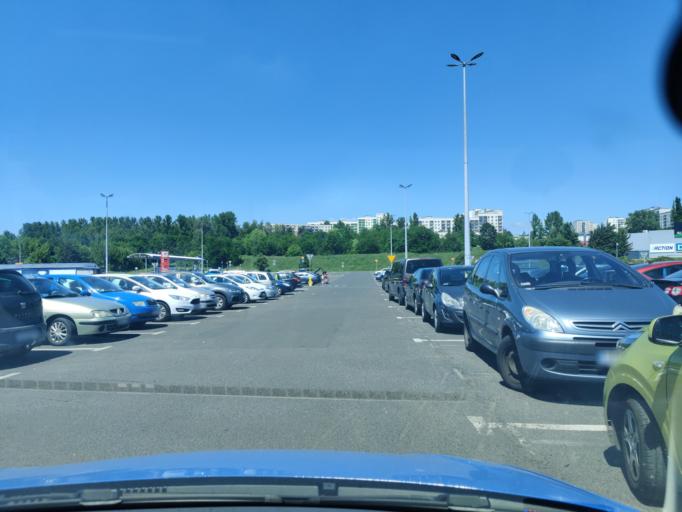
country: PL
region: Silesian Voivodeship
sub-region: Powiat bedzinski
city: Bedzin
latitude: 50.2913
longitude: 19.1515
